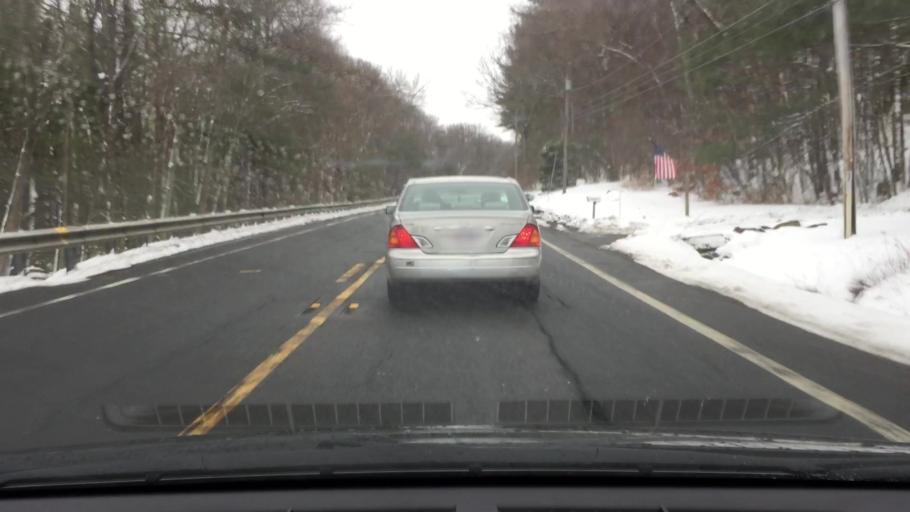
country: US
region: Massachusetts
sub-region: Hampshire County
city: Pelham
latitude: 42.3442
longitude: -72.4034
